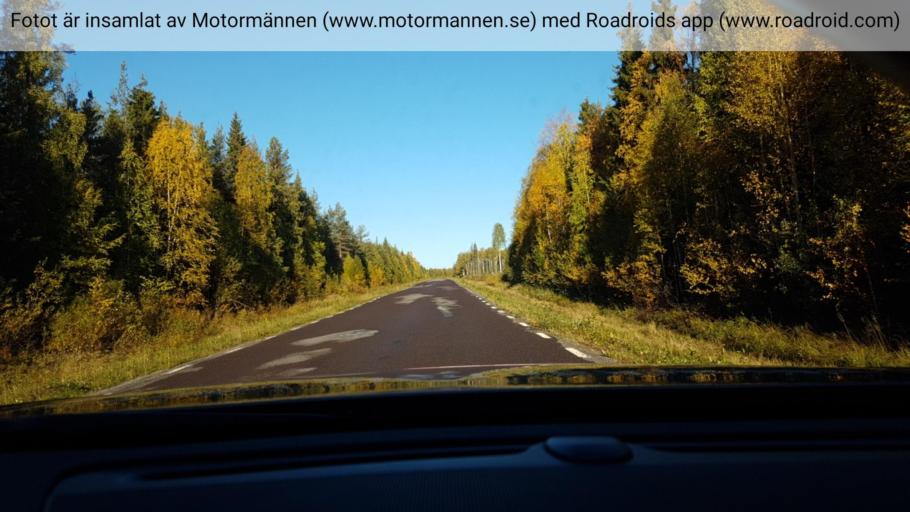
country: SE
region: Norrbotten
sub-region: Bodens Kommun
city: Boden
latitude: 66.0182
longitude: 21.5121
